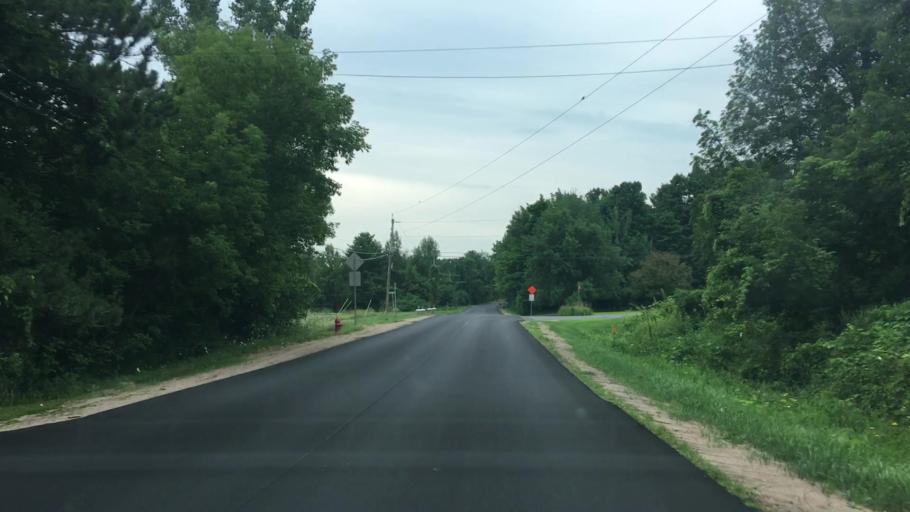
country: US
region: New York
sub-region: Clinton County
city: Peru
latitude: 44.5638
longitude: -73.5684
